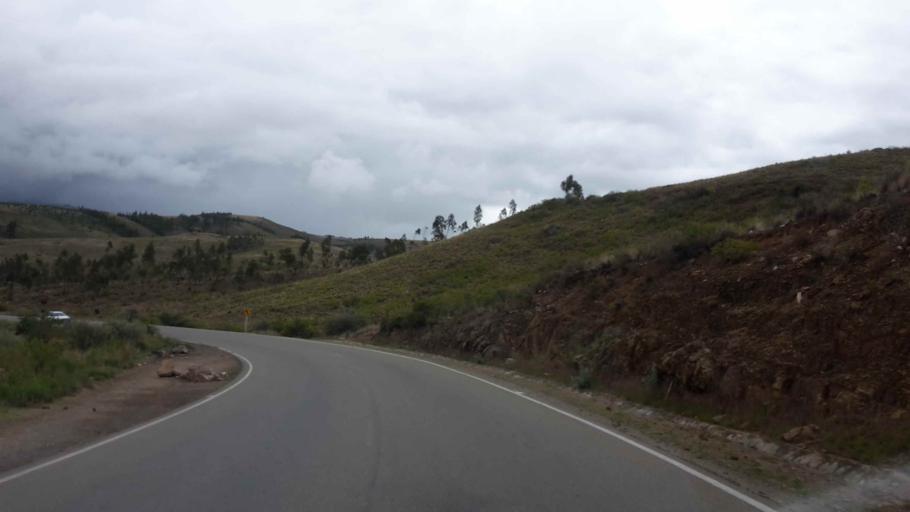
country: BO
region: Cochabamba
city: Arani
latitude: -17.4828
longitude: -65.7703
